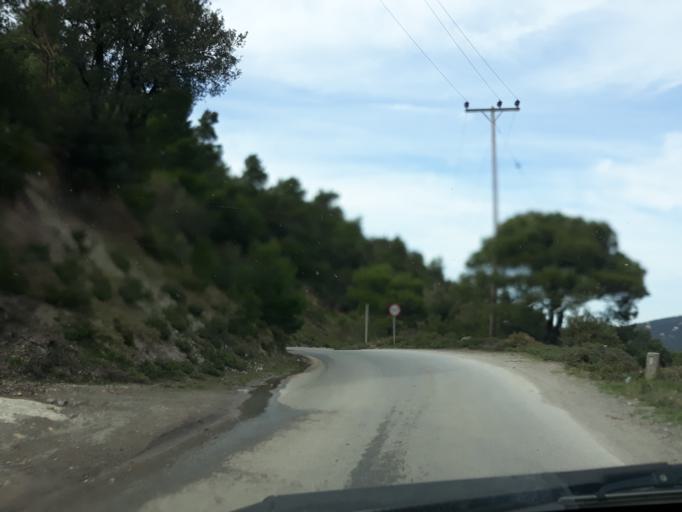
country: GR
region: Attica
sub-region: Nomarchia Anatolikis Attikis
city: Afidnes
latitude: 38.1831
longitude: 23.7929
